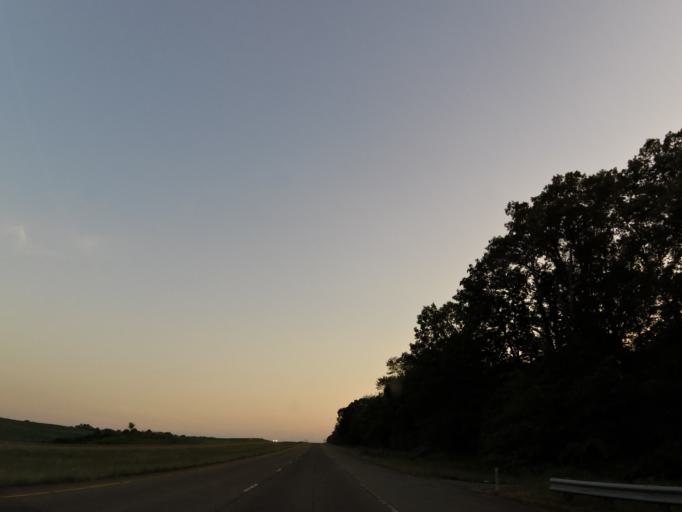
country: US
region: Tennessee
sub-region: Carroll County
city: McKenzie
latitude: 36.1542
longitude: -88.4687
